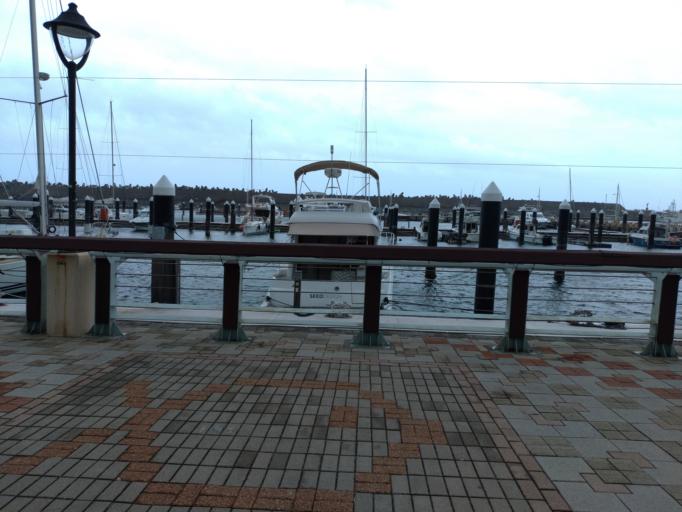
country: TW
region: Taiwan
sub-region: Keelung
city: Keelung
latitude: 25.1464
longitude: 121.7852
